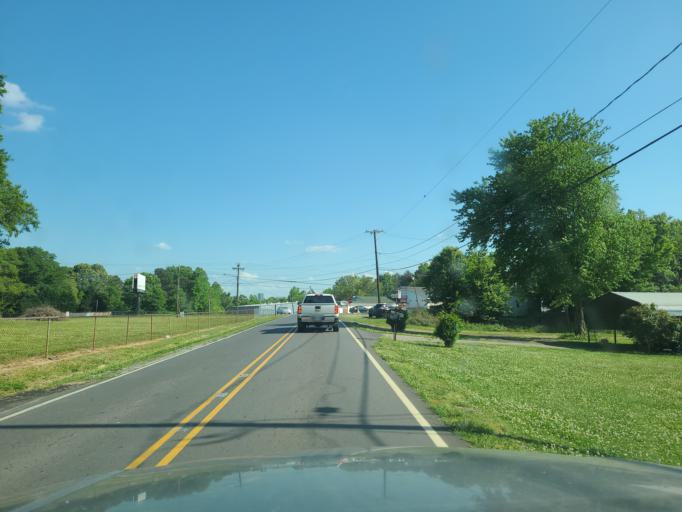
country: US
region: North Carolina
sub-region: Cleveland County
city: Shelby
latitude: 35.2260
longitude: -81.5284
